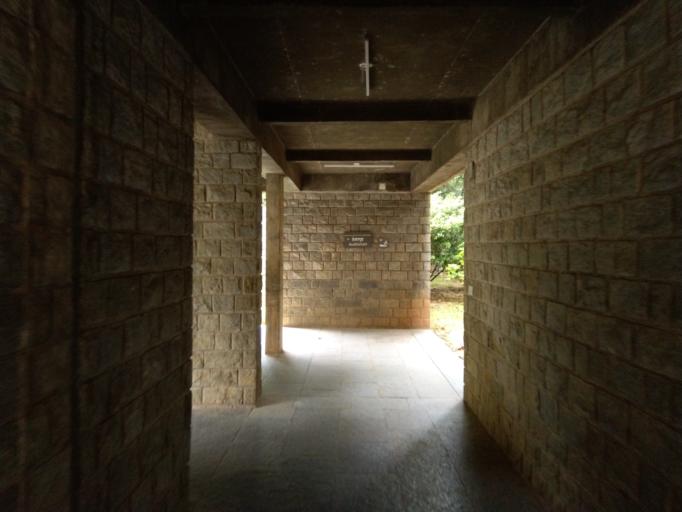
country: IN
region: Karnataka
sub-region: Bangalore Urban
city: Bangalore
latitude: 12.8943
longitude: 77.6012
